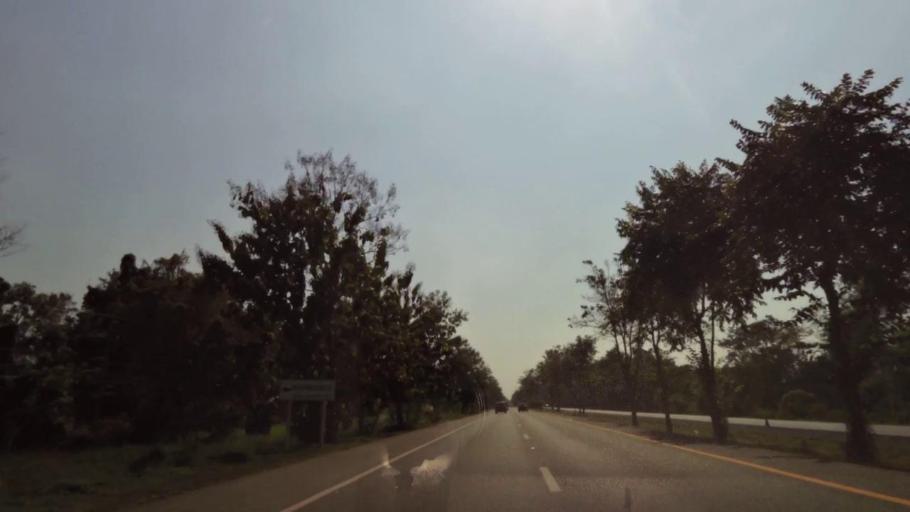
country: TH
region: Phichit
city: Bueng Na Rang
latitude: 16.0768
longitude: 100.1243
